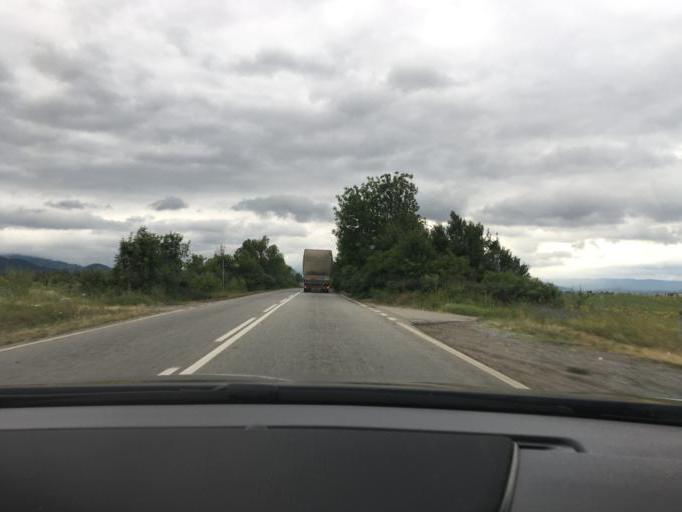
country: BG
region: Kyustendil
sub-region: Obshtina Kyustendil
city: Kyustendil
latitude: 42.2714
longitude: 22.7768
